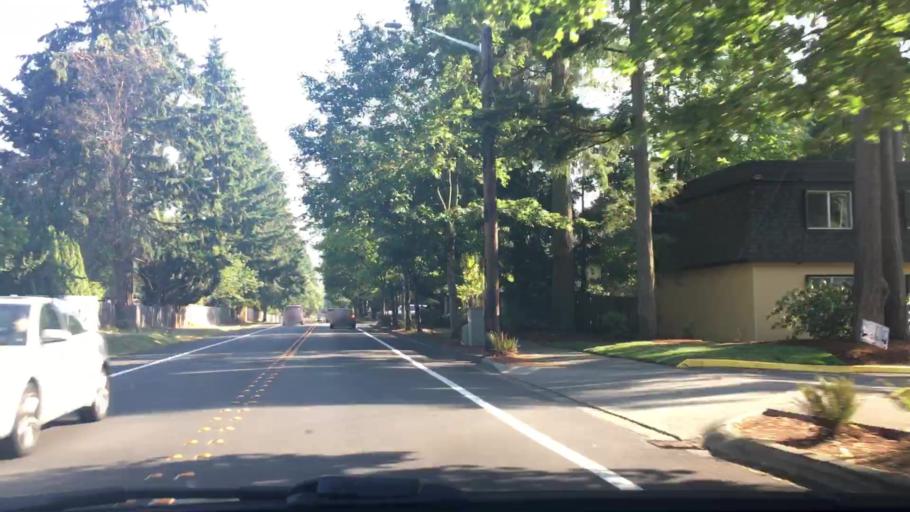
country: US
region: Washington
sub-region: King County
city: Sammamish
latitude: 47.6226
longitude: -122.1217
